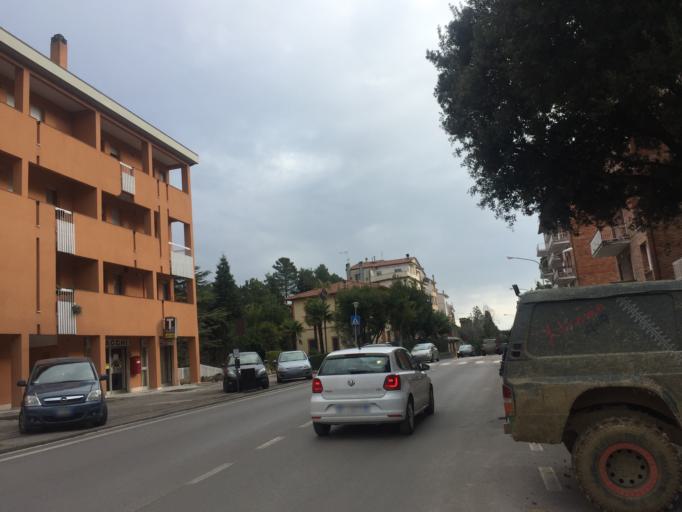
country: IT
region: Umbria
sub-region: Provincia di Perugia
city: Perugia
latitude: 43.1189
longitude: 12.4027
